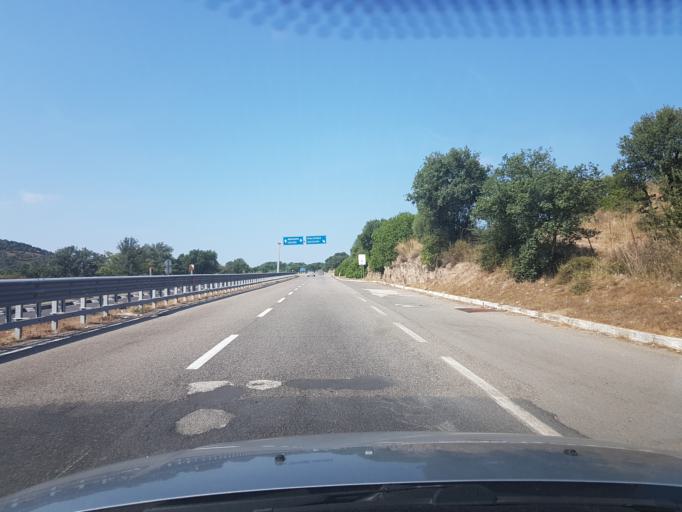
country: IT
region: Sardinia
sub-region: Provincia di Nuoro
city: Oniferi
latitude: 40.3066
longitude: 9.1940
